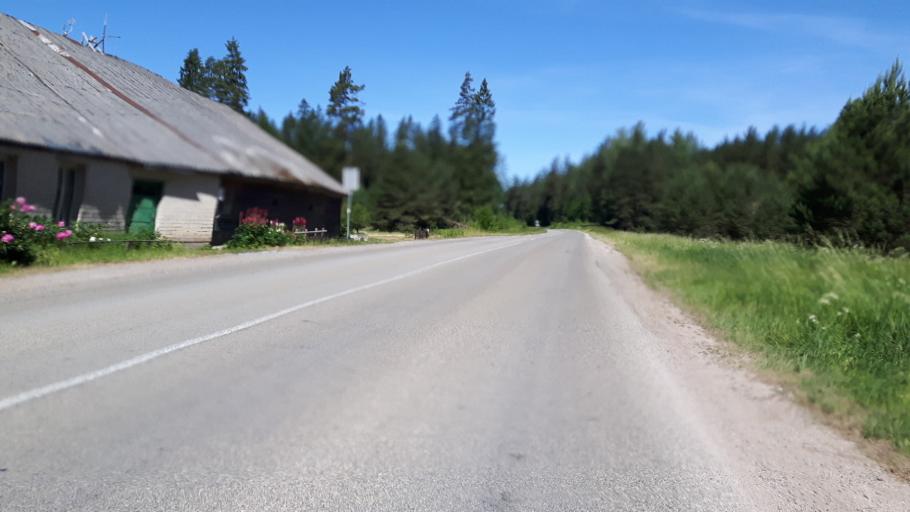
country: LV
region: Tukuma Rajons
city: Tukums
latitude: 57.0119
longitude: 23.0517
